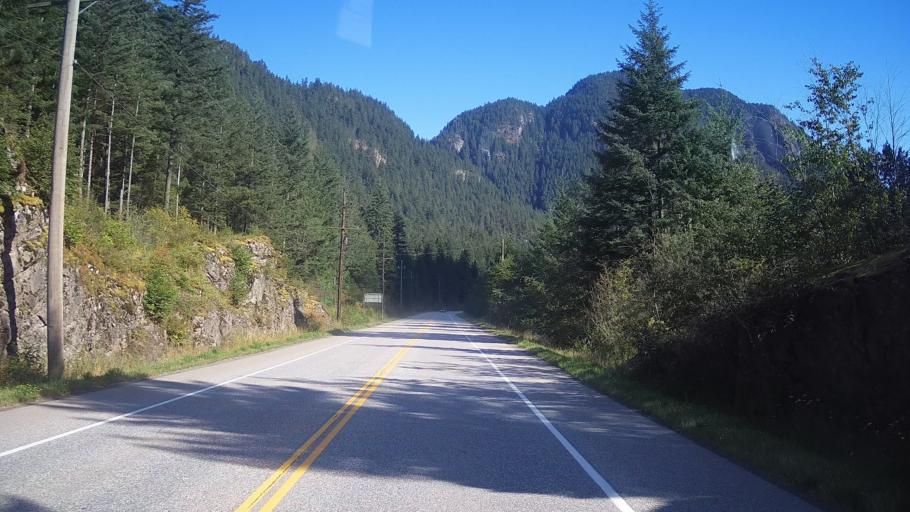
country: CA
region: British Columbia
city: Hope
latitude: 49.5981
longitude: -121.4144
